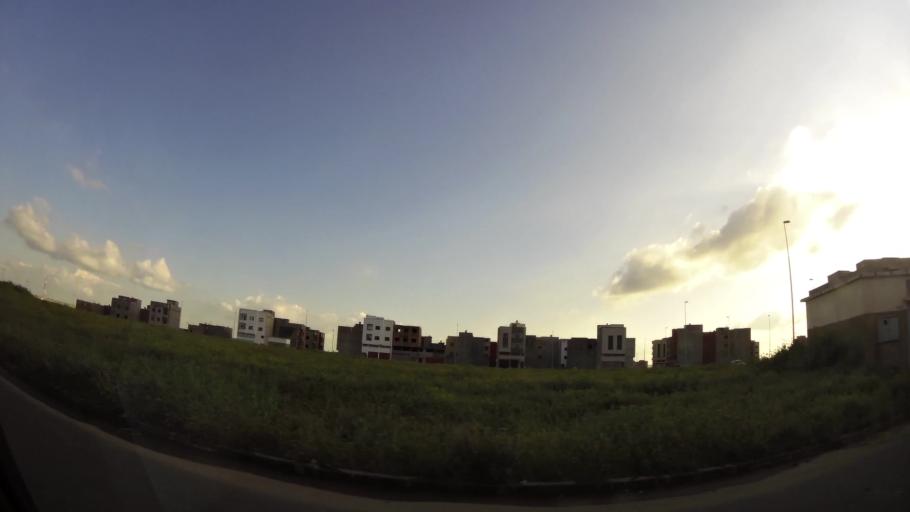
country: MA
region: Chaouia-Ouardigha
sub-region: Settat Province
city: Settat
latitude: 32.9924
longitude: -7.6336
